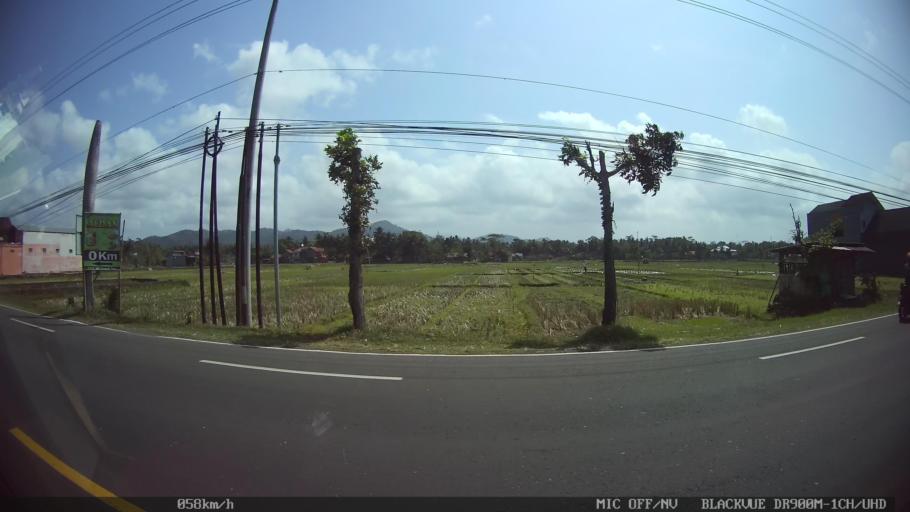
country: ID
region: Daerah Istimewa Yogyakarta
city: Srandakan
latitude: -7.8894
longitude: 110.1006
